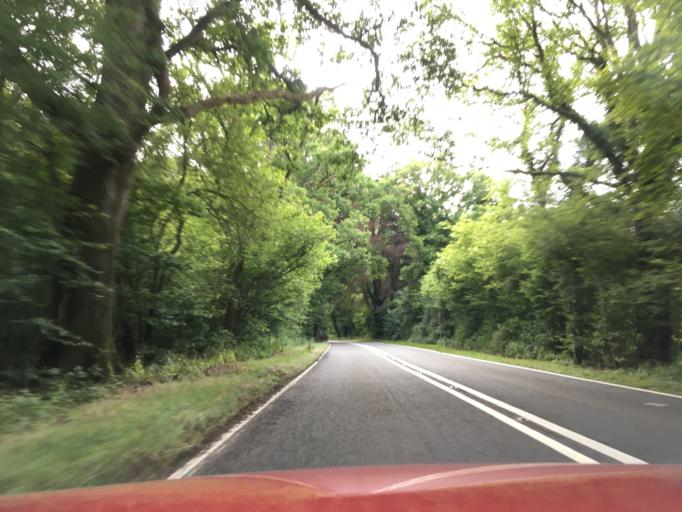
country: GB
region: England
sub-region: Hampshire
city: Four Marks
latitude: 51.0360
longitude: -1.0923
